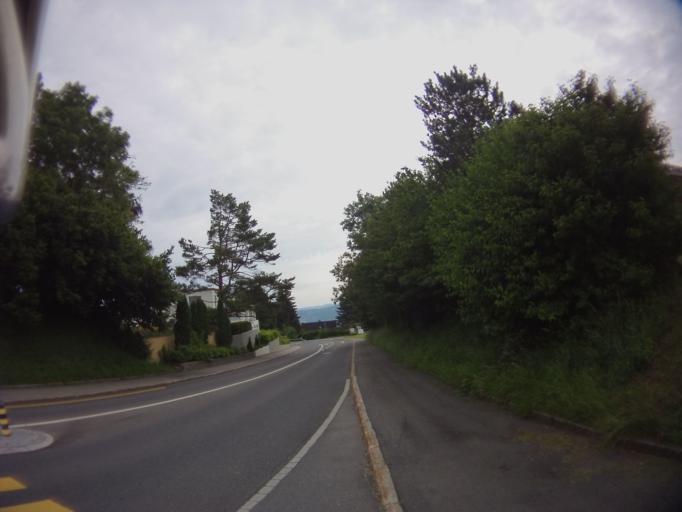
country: CH
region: Zurich
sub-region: Bezirk Horgen
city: Muehlehalde
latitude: 47.2760
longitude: 8.5215
